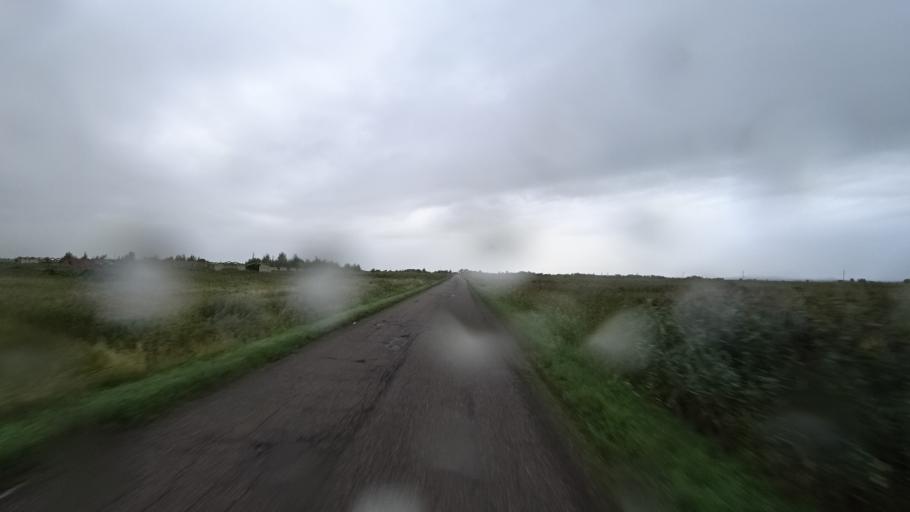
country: RU
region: Primorskiy
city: Chernigovka
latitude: 44.3896
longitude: 132.5294
